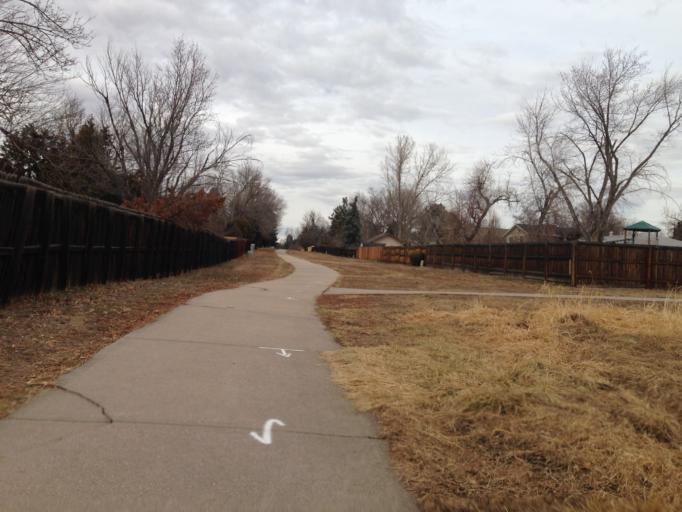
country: US
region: Colorado
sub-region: Adams County
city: Westminster
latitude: 39.8495
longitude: -105.0627
